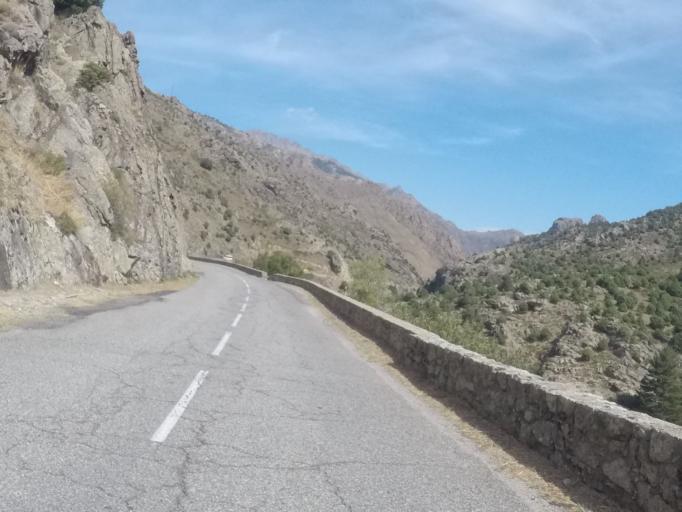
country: FR
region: Corsica
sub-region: Departement de la Haute-Corse
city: Corte
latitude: 42.3477
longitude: 9.0492
